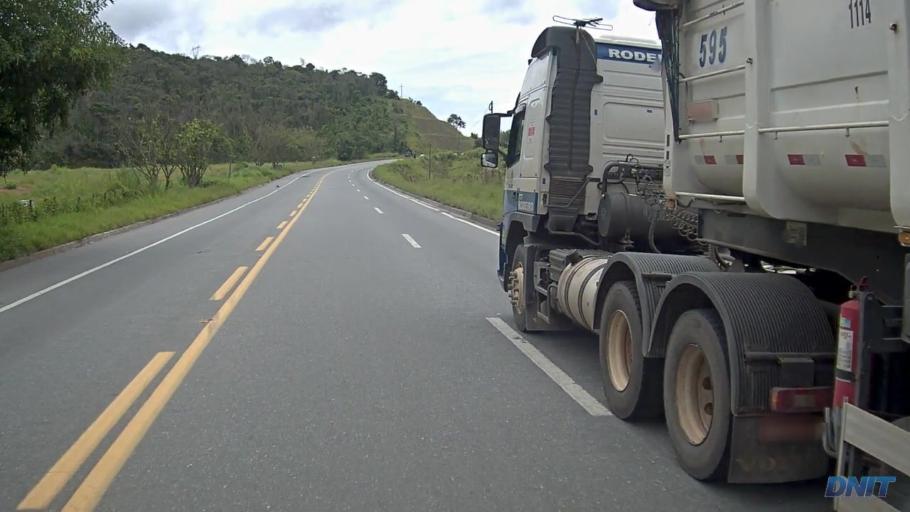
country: BR
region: Minas Gerais
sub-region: Nova Era
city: Nova Era
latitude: -19.7028
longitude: -42.9973
